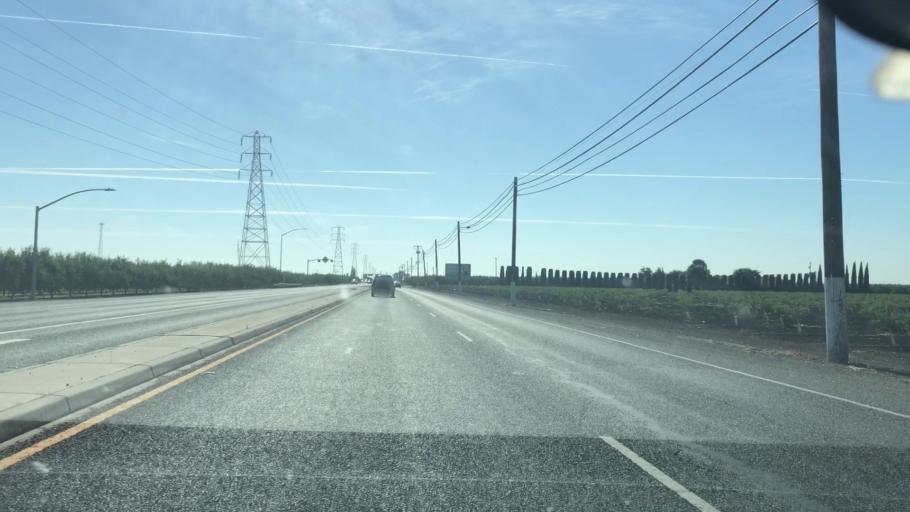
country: US
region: California
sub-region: San Joaquin County
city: Tracy
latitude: 37.7397
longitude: -121.3793
